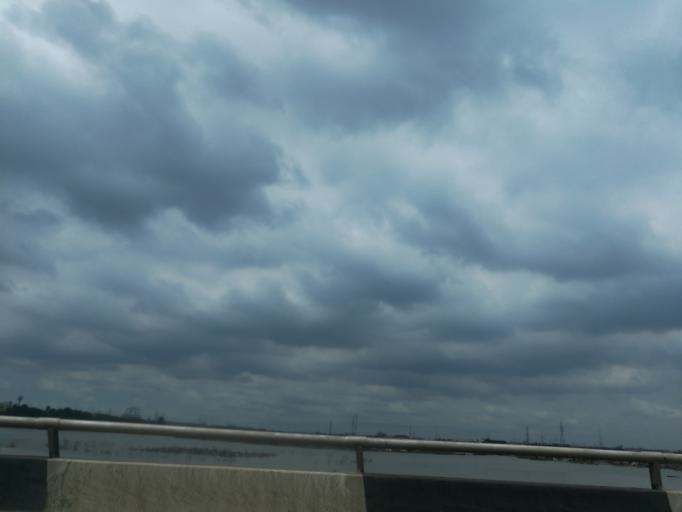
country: NG
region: Lagos
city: Somolu
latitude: 6.5262
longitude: 3.4033
